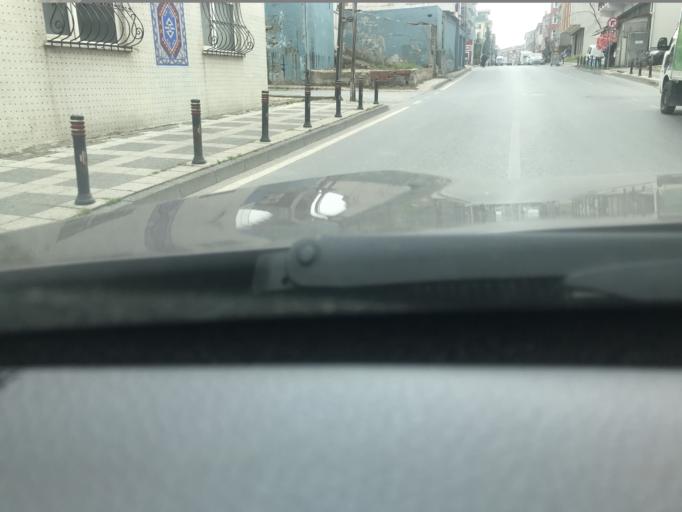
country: TR
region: Istanbul
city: Umraniye
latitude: 41.0251
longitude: 29.1321
